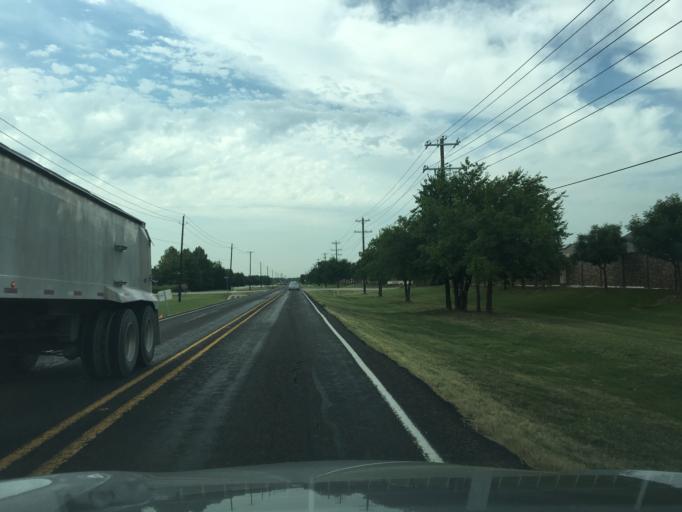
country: US
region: Texas
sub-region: Collin County
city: Parker
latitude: 33.0769
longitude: -96.6202
